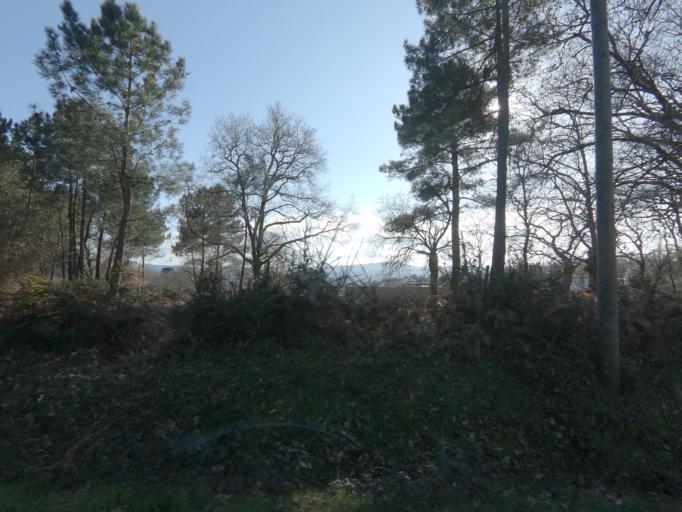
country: ES
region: Galicia
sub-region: Provincia da Coruna
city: Ribeira
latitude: 42.7133
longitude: -8.4447
